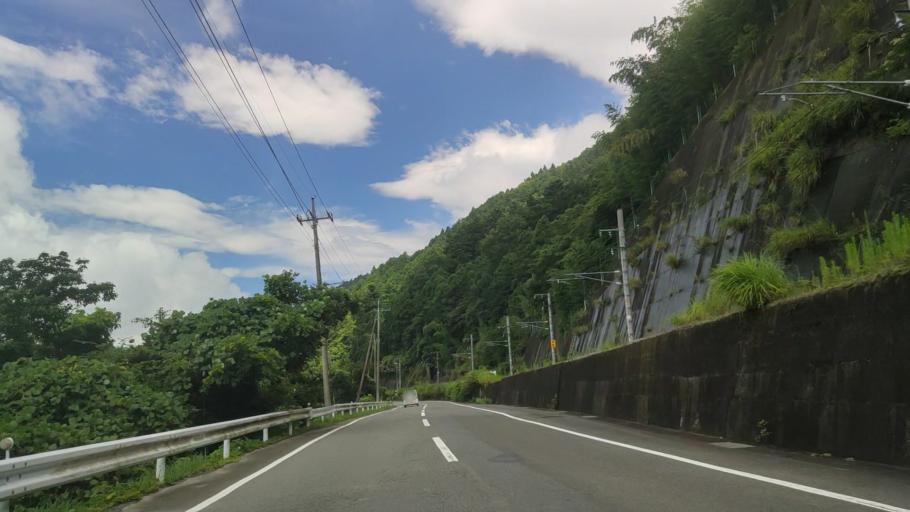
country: JP
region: Shizuoka
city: Fujinomiya
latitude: 35.2619
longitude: 138.4782
